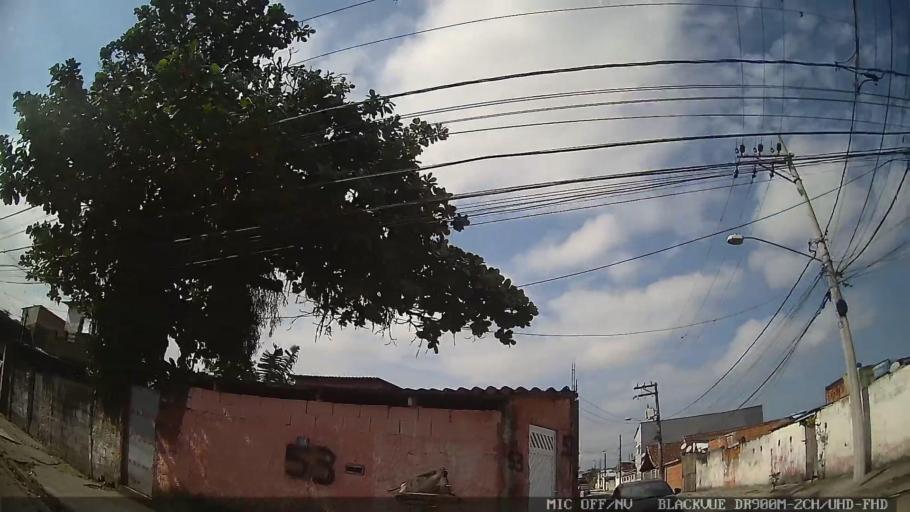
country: BR
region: Sao Paulo
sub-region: Santos
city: Santos
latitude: -23.9539
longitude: -46.2950
